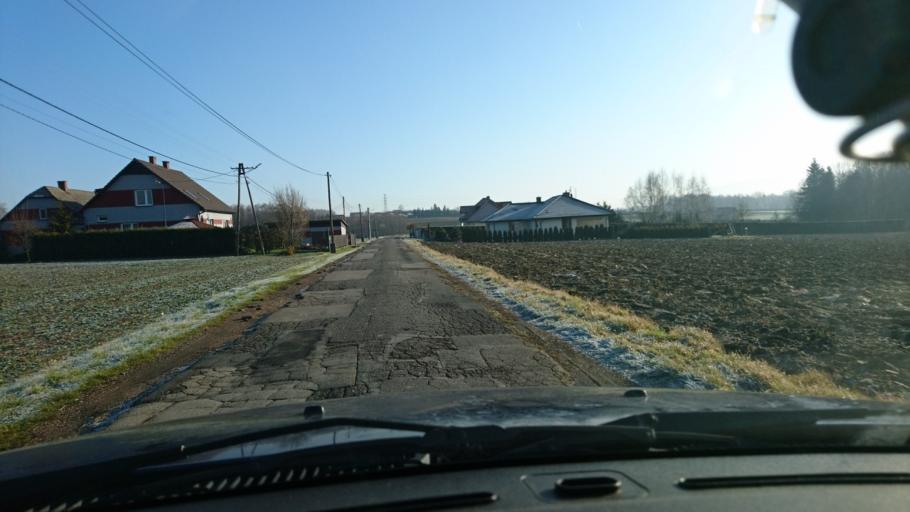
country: PL
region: Silesian Voivodeship
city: Janowice
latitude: 49.9008
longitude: 19.0834
